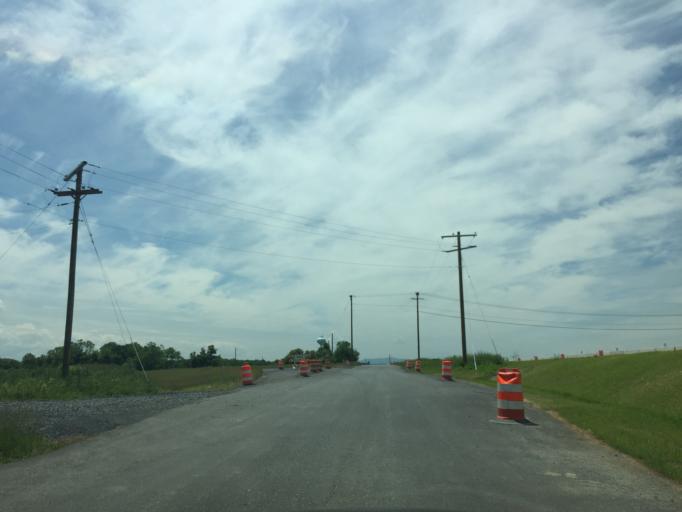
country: US
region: Virginia
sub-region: Frederick County
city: Stephens City
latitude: 39.1240
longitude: -78.1878
